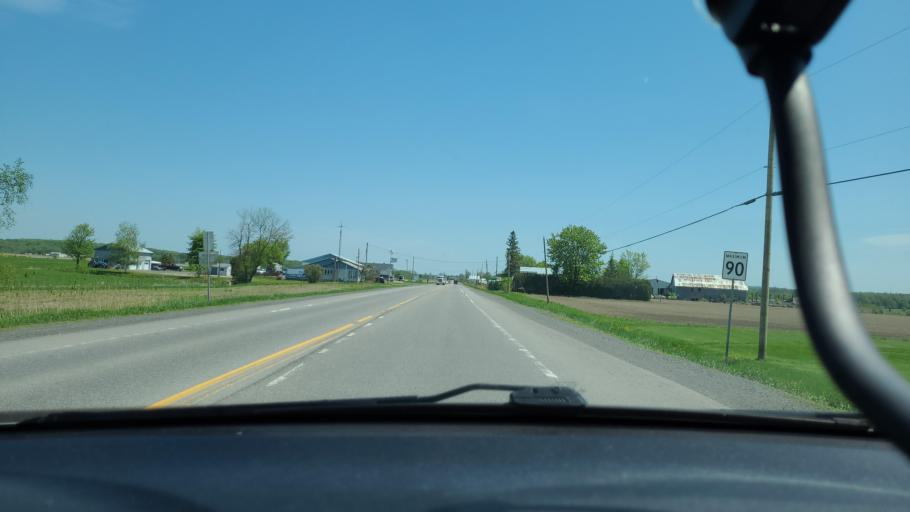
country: CA
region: Quebec
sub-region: Laurentides
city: Mirabel
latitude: 45.6285
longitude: -74.1202
